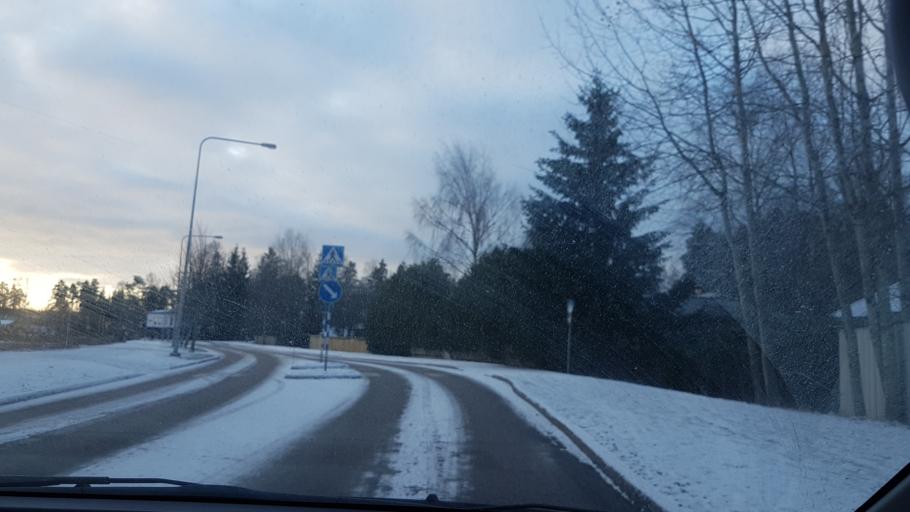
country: FI
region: Uusimaa
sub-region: Helsinki
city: Helsinki
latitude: 60.2828
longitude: 24.9078
